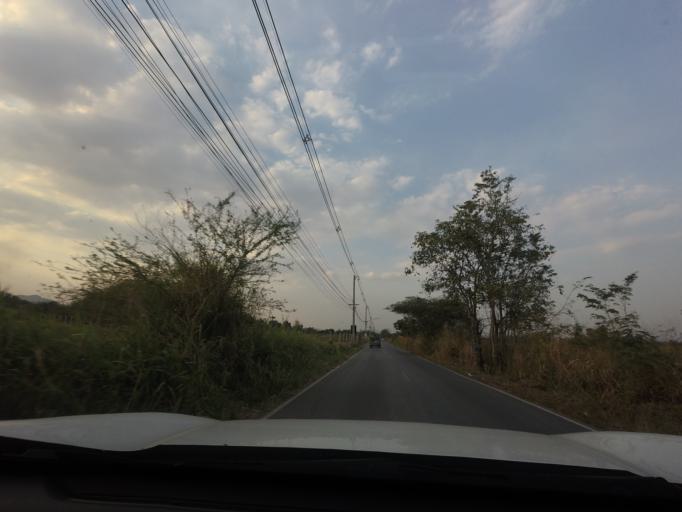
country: TH
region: Nakhon Ratchasima
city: Pak Chong
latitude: 14.5976
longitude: 101.4453
